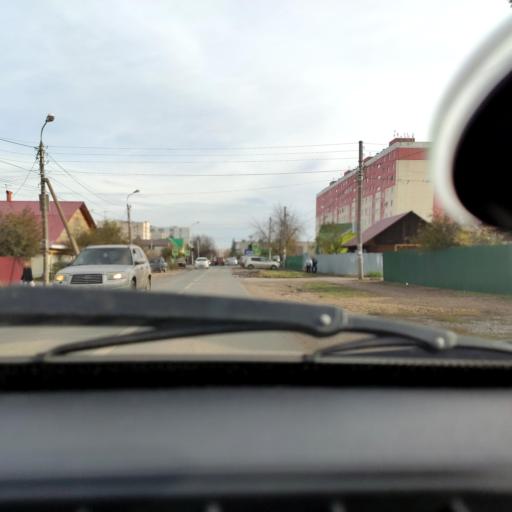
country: RU
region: Bashkortostan
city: Avdon
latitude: 54.7083
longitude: 55.8189
